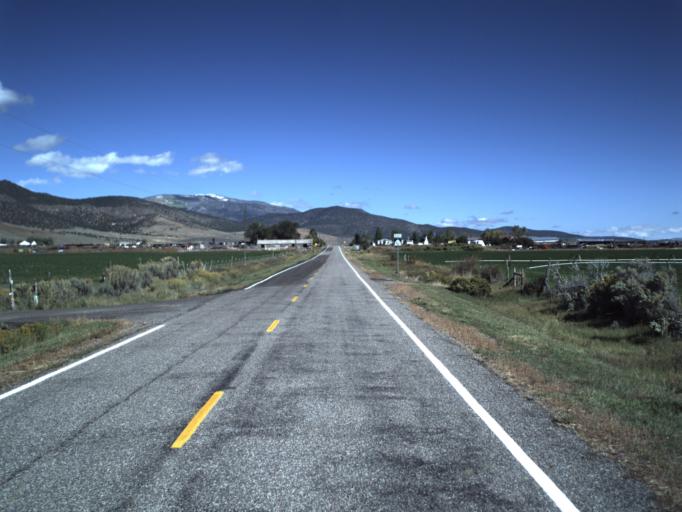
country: US
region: Utah
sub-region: Wayne County
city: Loa
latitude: 38.4254
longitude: -111.9227
